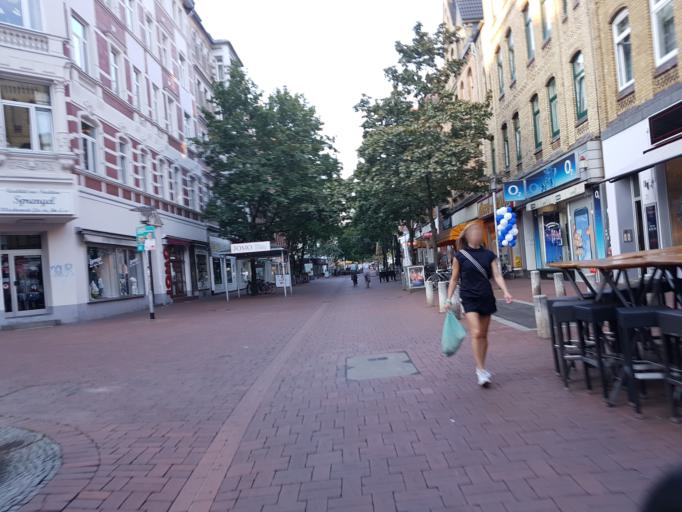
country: DE
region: Lower Saxony
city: Hannover
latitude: 52.3871
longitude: 9.7490
